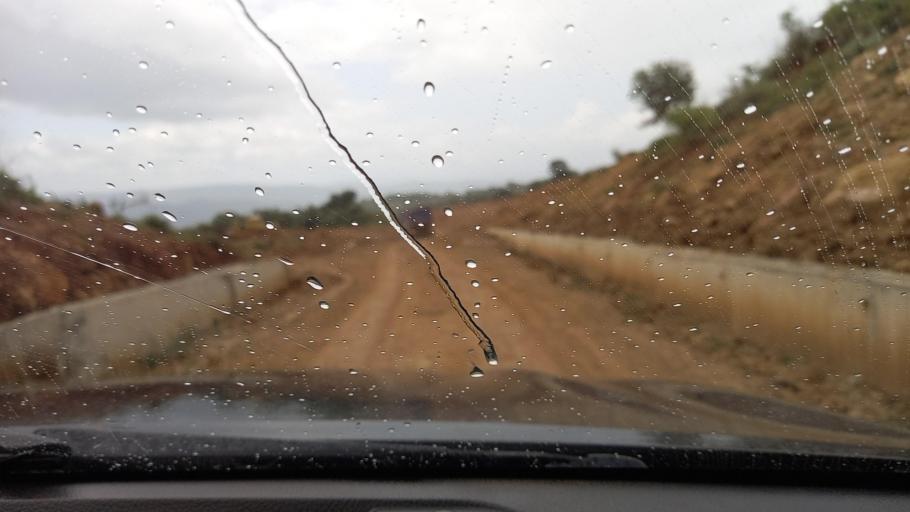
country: ET
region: Southern Nations, Nationalities, and People's Region
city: Mizan Teferi
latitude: 6.1742
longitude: 35.7134
